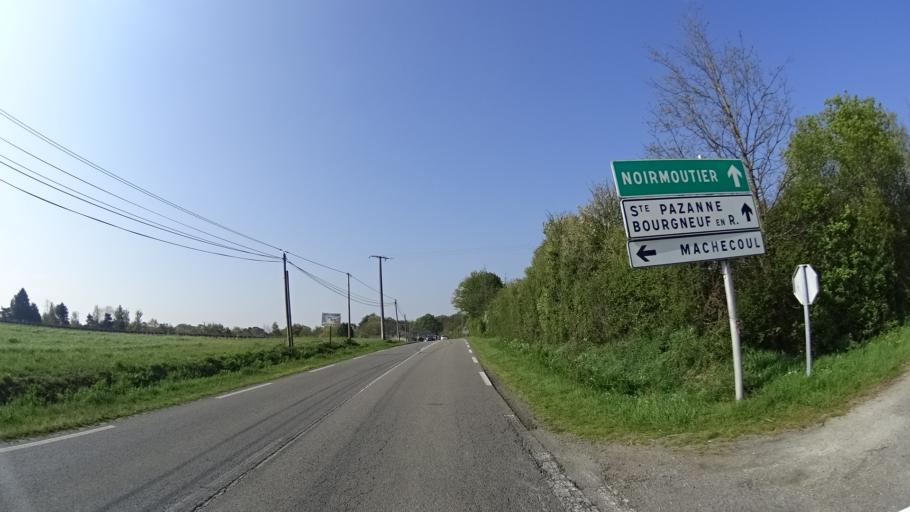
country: FR
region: Pays de la Loire
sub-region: Departement de la Loire-Atlantique
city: Sainte-Pazanne
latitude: 47.1075
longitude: -1.7881
